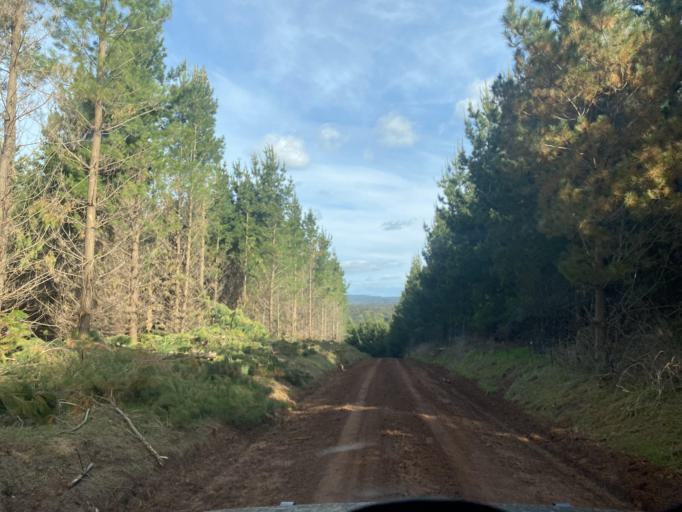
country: AU
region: Victoria
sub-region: Mansfield
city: Mansfield
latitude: -36.8368
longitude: 146.1789
